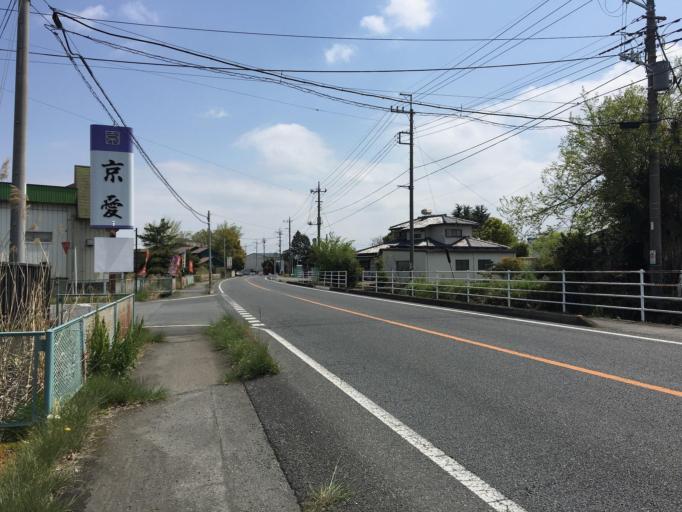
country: JP
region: Gunma
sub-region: Sawa-gun
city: Tamamura
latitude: 36.2897
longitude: 139.1490
